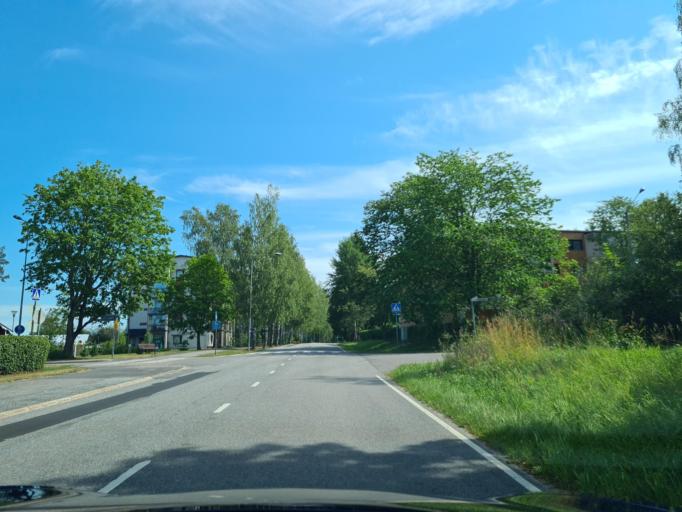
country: FI
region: Varsinais-Suomi
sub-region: Turku
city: Paimio
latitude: 60.4507
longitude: 22.6949
